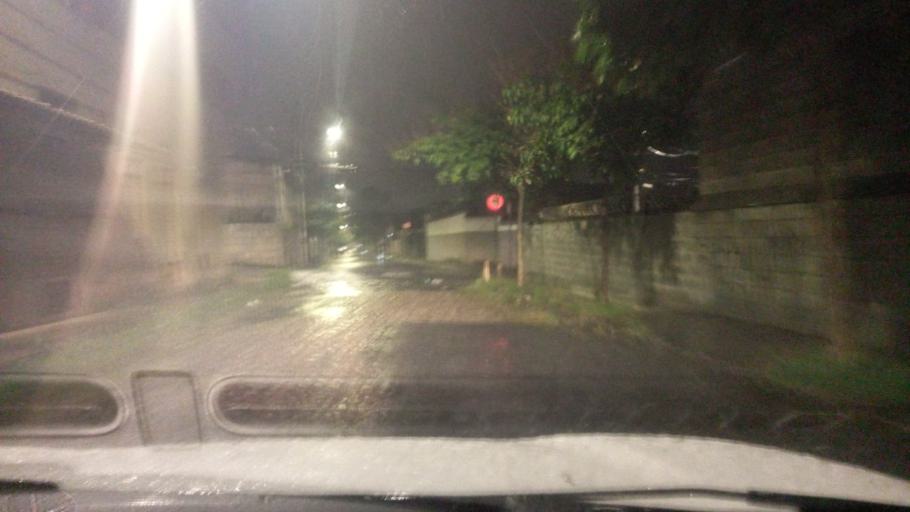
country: BR
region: Minas Gerais
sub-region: Belo Horizonte
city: Belo Horizonte
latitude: -19.9126
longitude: -43.9695
